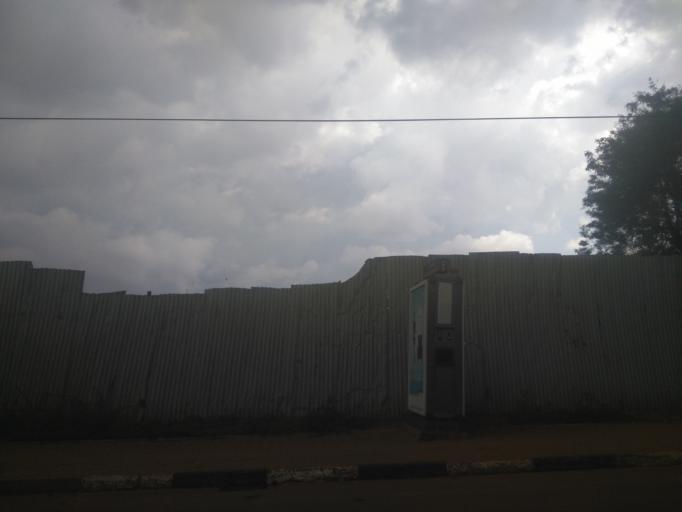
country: UG
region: Central Region
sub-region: Kampala District
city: Kampala
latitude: 0.3175
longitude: 32.5897
